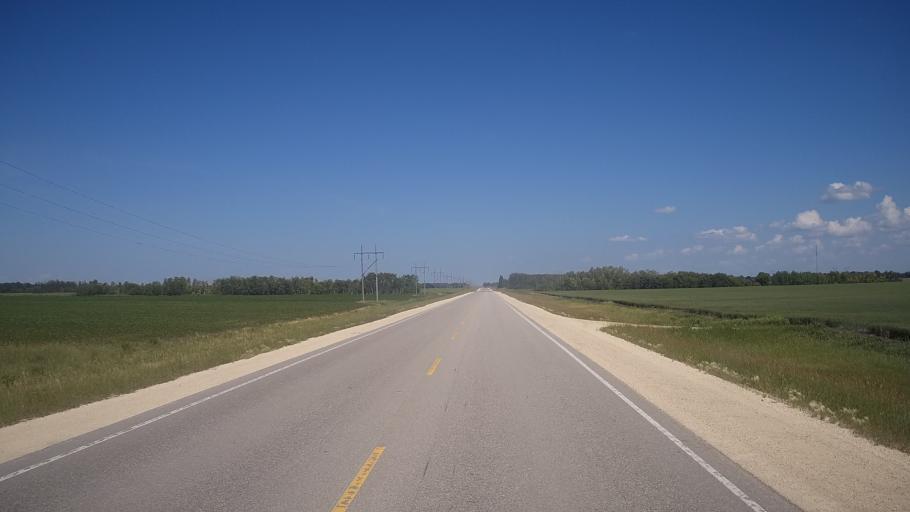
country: CA
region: Manitoba
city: Stonewall
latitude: 50.1227
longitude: -97.3741
